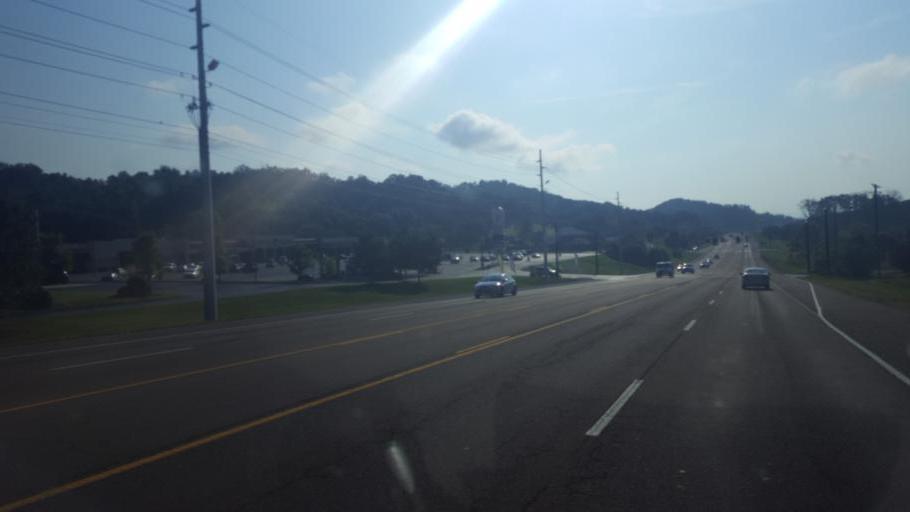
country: US
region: Tennessee
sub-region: Sullivan County
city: Blountville
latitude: 36.5243
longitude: -82.3158
